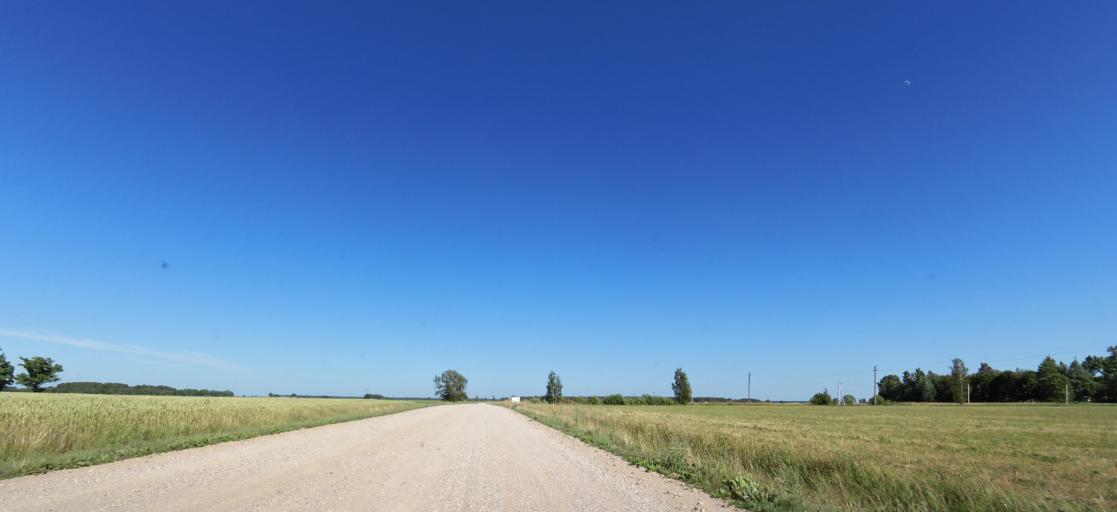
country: LT
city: Vabalninkas
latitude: 56.0264
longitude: 24.6715
